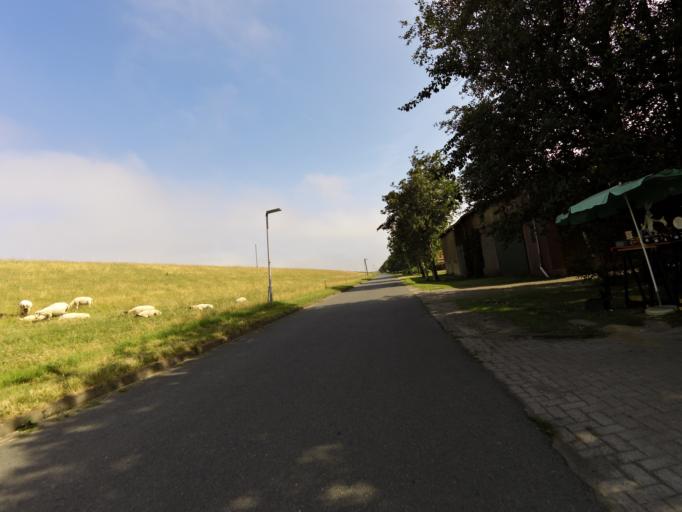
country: DE
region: Lower Saxony
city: Nordholz
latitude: 53.7885
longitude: 8.5546
